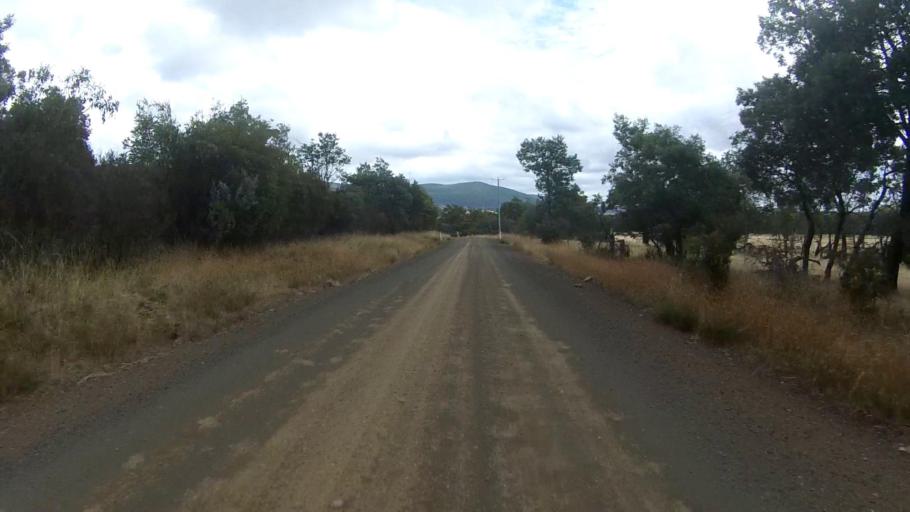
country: AU
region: Tasmania
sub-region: Break O'Day
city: St Helens
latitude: -41.8220
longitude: 147.9887
